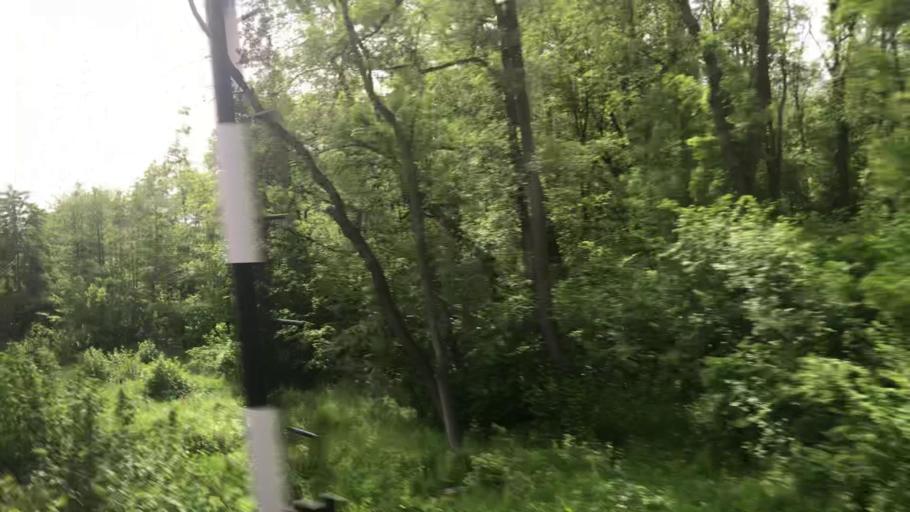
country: PL
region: Lower Silesian Voivodeship
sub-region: Powiat wroclawski
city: Katy Wroclawskie
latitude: 51.0086
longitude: 16.6964
